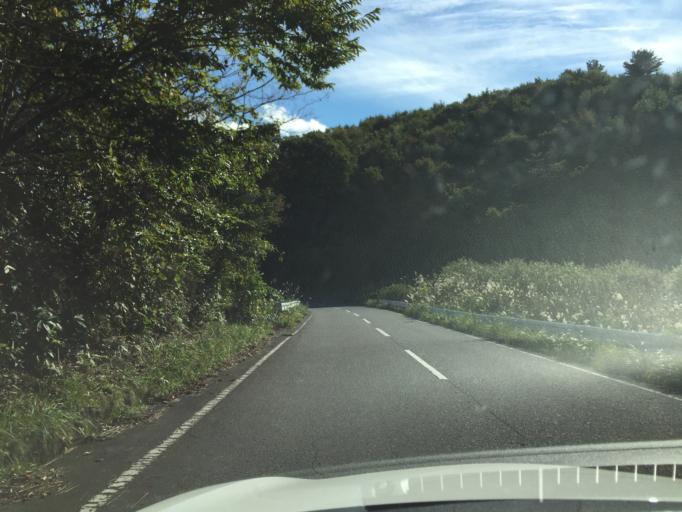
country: JP
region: Fukushima
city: Ishikawa
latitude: 37.1539
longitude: 140.5961
